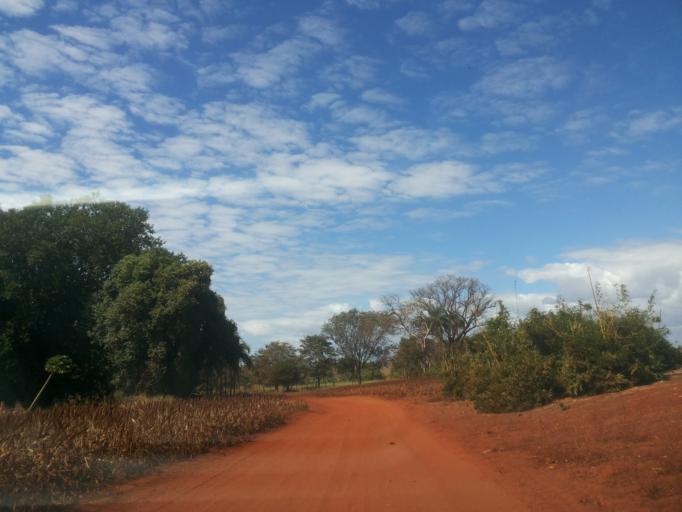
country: BR
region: Minas Gerais
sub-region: Centralina
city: Centralina
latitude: -18.5579
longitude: -49.2340
